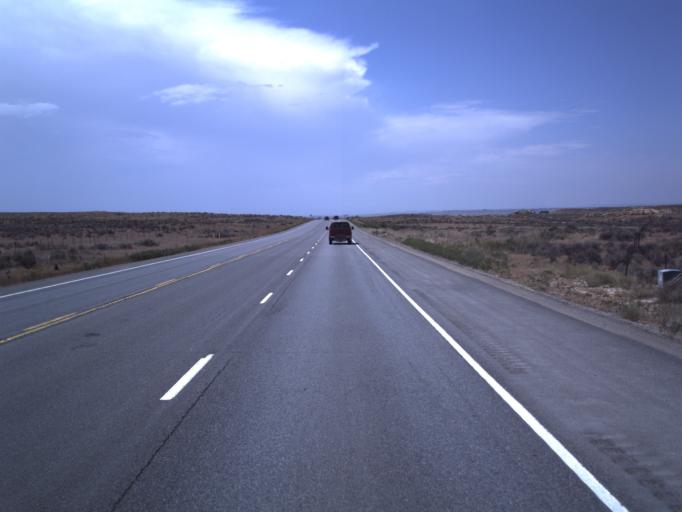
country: US
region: Utah
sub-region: Uintah County
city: Maeser
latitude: 40.3106
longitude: -109.7501
